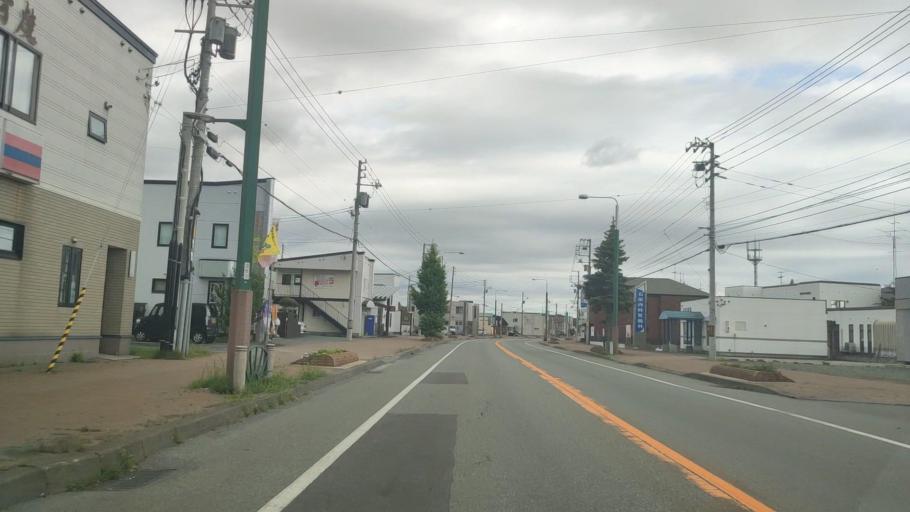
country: JP
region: Hokkaido
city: Date
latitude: 42.5501
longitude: 140.7637
